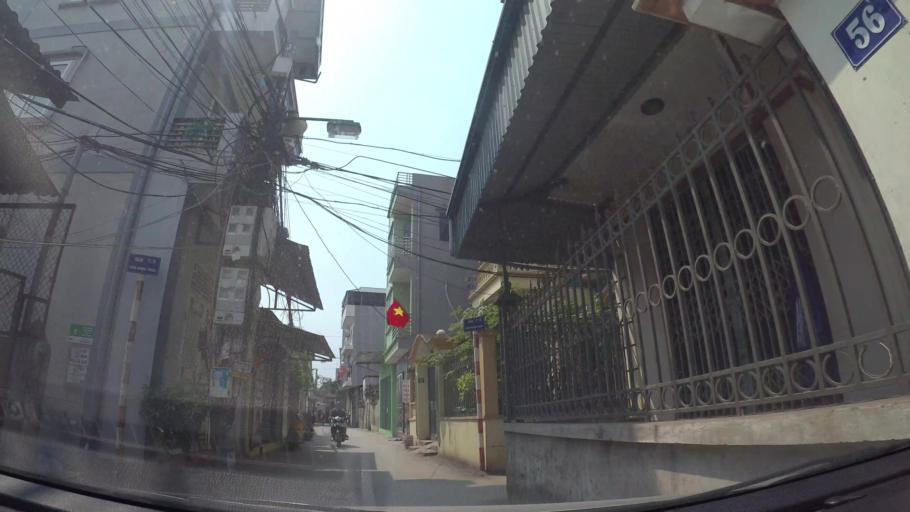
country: VN
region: Ha Noi
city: Ha Dong
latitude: 20.9911
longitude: 105.7710
